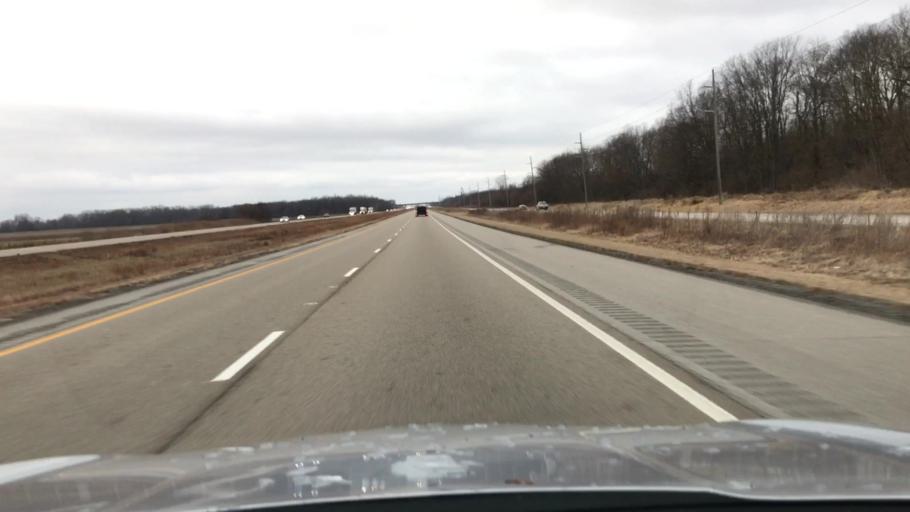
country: US
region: Illinois
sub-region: Logan County
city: Atlanta
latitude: 40.2329
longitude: -89.2642
